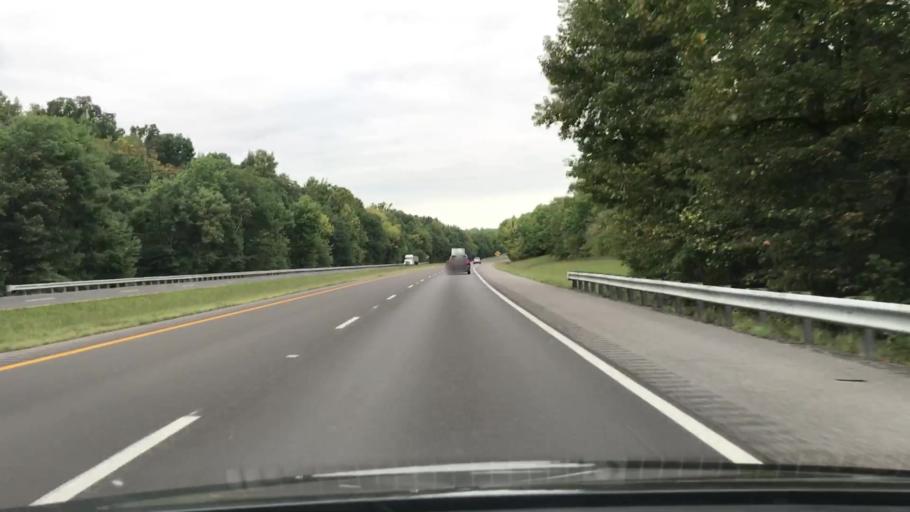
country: US
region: Kentucky
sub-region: Fulton County
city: Fulton
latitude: 36.6047
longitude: -88.7958
